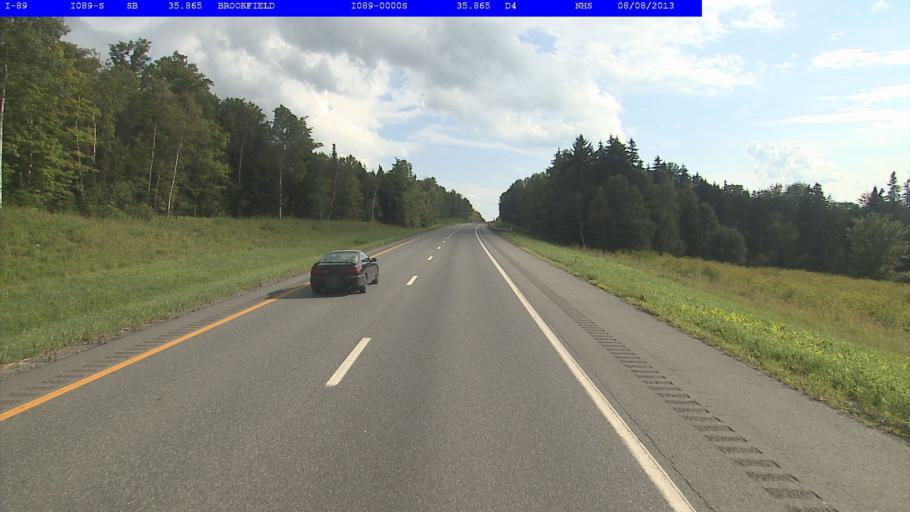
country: US
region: Vermont
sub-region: Orange County
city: Randolph
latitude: 44.0162
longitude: -72.6185
